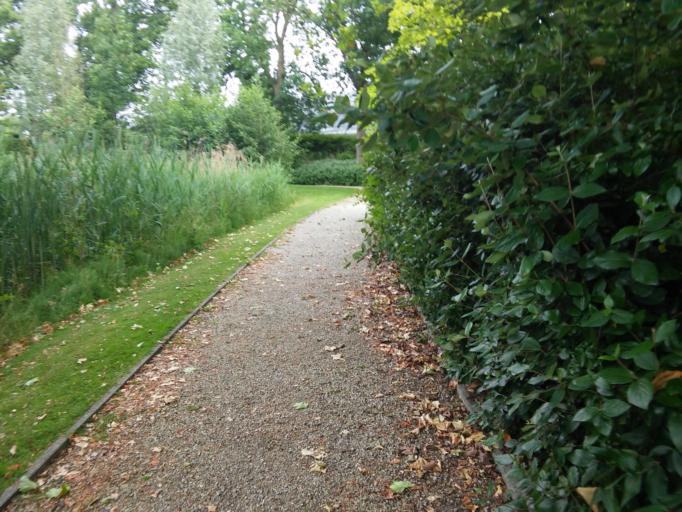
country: BE
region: Flanders
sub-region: Provincie Antwerpen
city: Rumst
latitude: 51.0745
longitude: 4.4242
